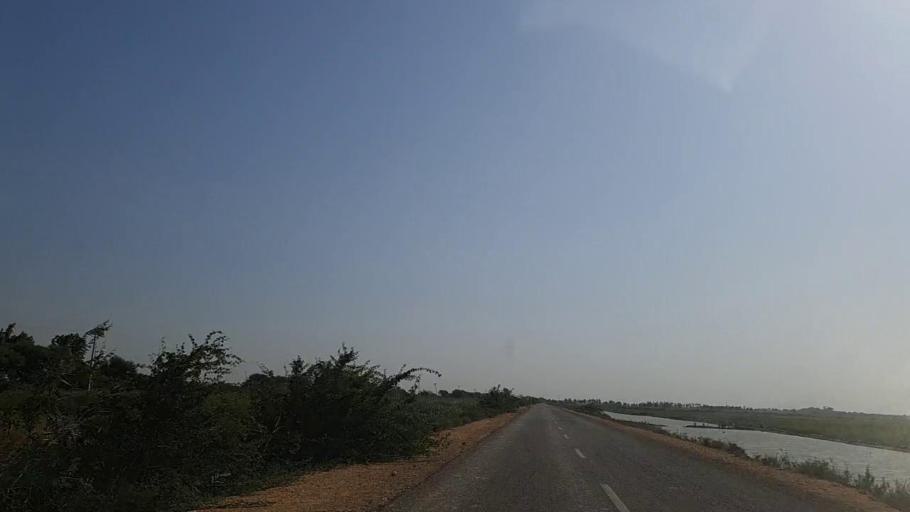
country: PK
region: Sindh
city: Jati
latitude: 24.4997
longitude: 68.2747
